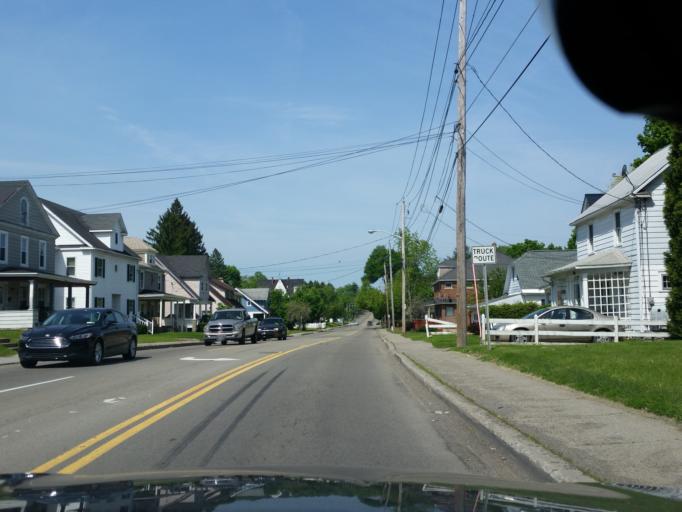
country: US
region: New York
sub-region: Chautauqua County
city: Jamestown West
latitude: 42.0971
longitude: -79.2620
